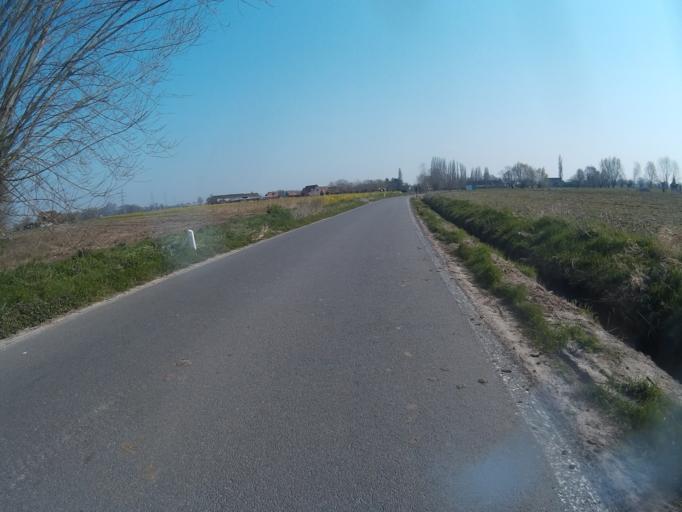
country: BE
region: Flanders
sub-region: Provincie Oost-Vlaanderen
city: Zomergem
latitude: 51.1111
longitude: 3.5184
